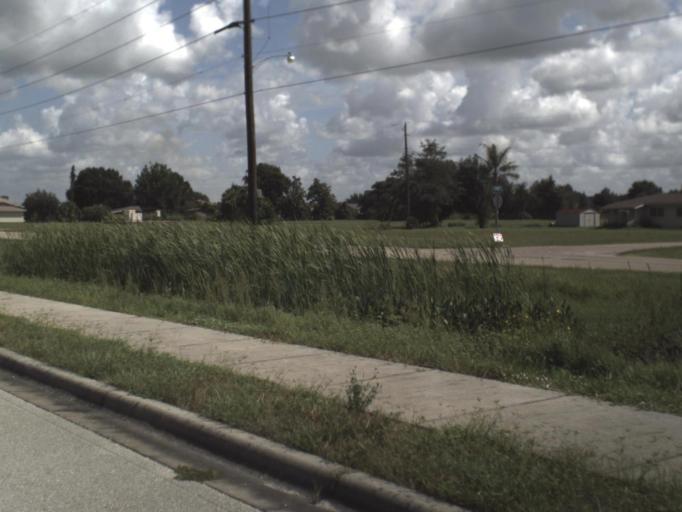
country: US
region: Florida
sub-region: Charlotte County
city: Cleveland
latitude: 26.9896
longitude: -81.9590
